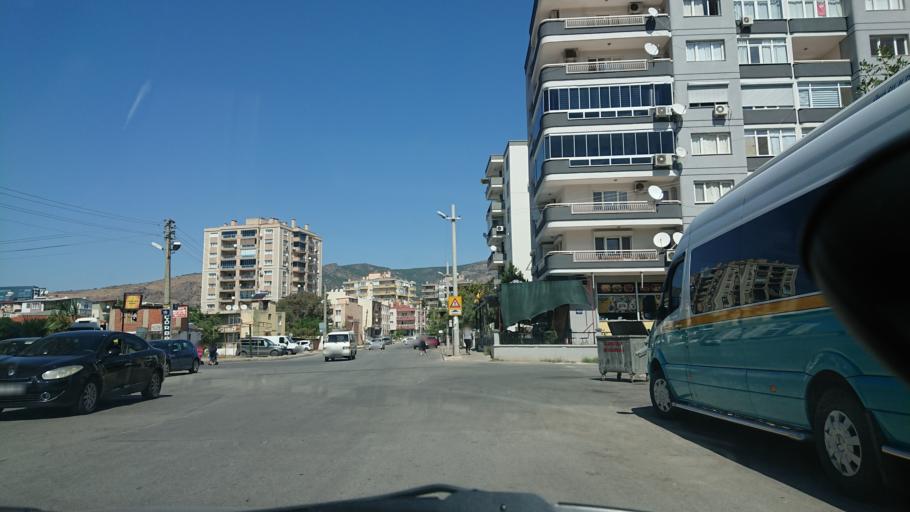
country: TR
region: Izmir
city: Karsiyaka
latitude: 38.4797
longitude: 27.1175
